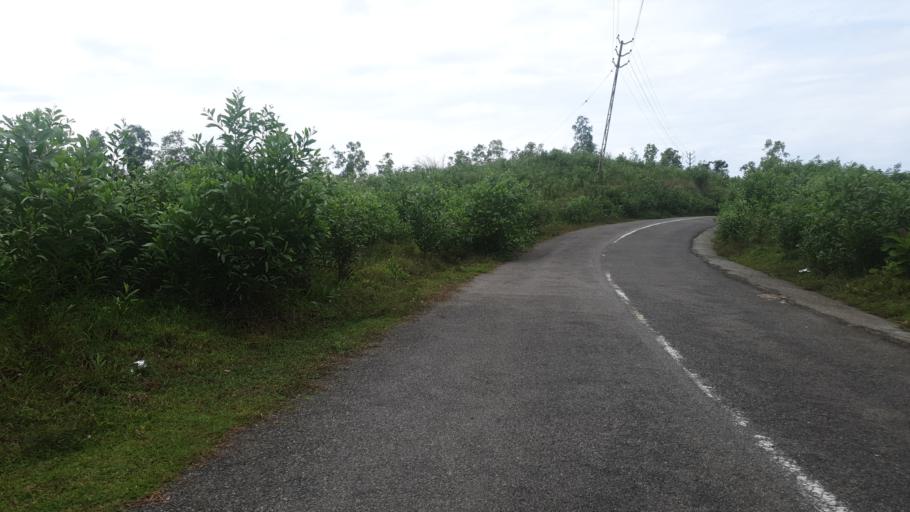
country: IN
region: Kerala
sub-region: Thiruvananthapuram
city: Nedumangad
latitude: 8.6402
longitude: 77.1095
